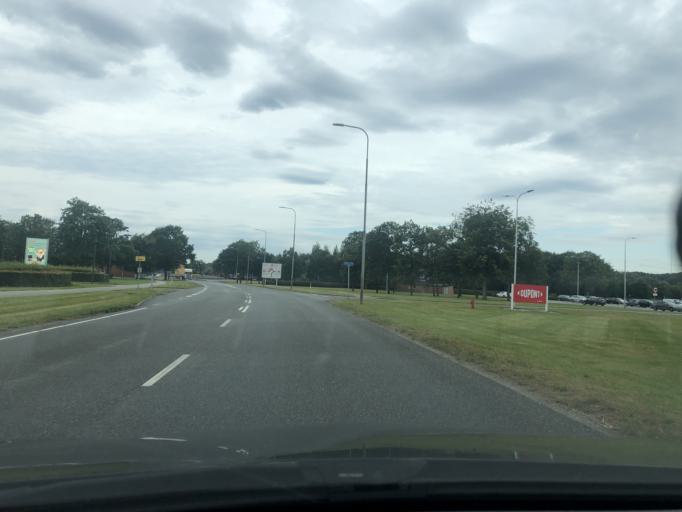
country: DK
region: South Denmark
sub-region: Billund Kommune
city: Grindsted
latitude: 55.7624
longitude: 8.9337
